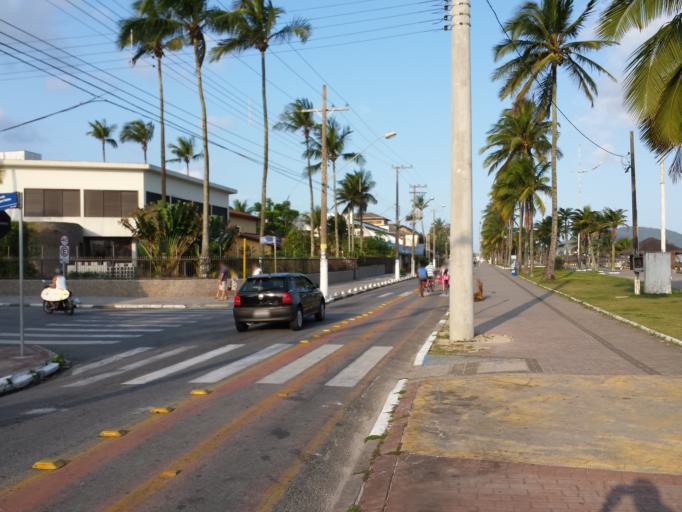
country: BR
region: Sao Paulo
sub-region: Guaruja
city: Guaruja
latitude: -23.9893
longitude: -46.2395
